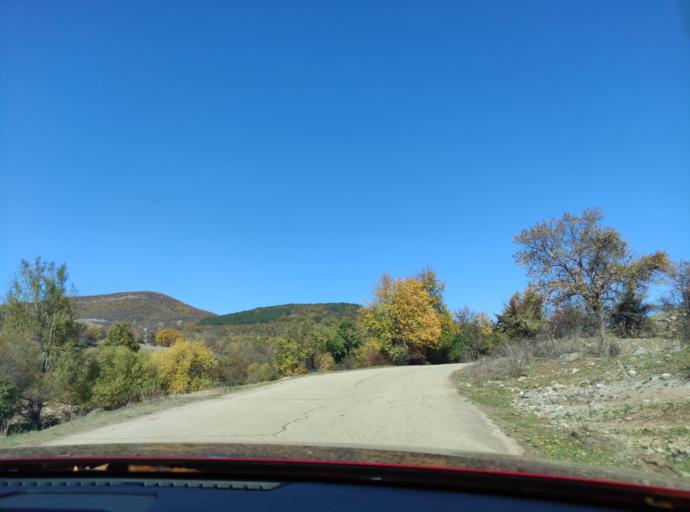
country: BG
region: Montana
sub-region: Obshtina Chiprovtsi
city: Chiprovtsi
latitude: 43.4491
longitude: 23.0462
